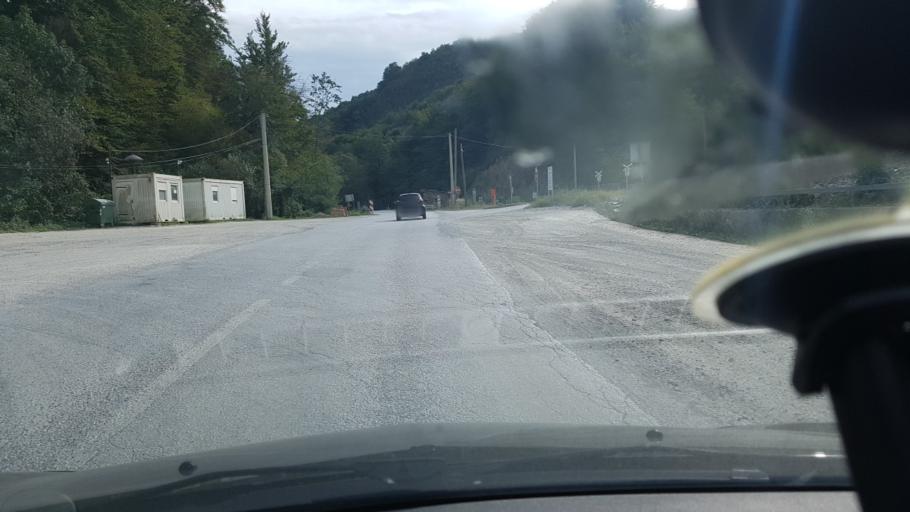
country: HR
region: Krapinsko-Zagorska
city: Mihovljan
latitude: 46.1860
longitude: 15.9845
